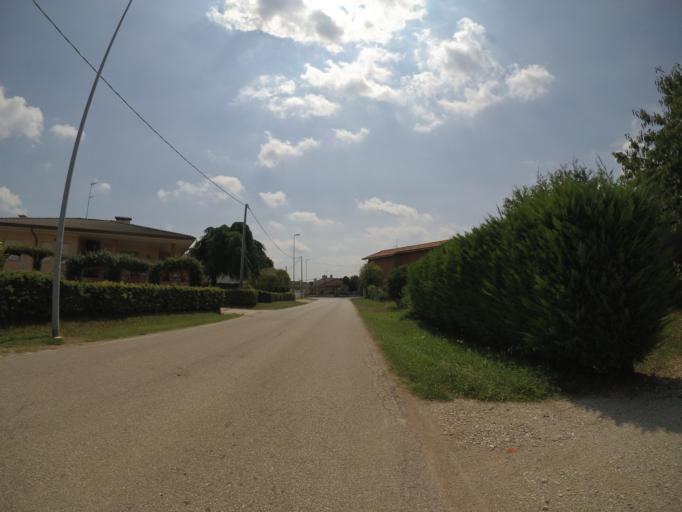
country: IT
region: Friuli Venezia Giulia
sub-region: Provincia di Udine
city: Basiliano
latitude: 45.9823
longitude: 13.0946
